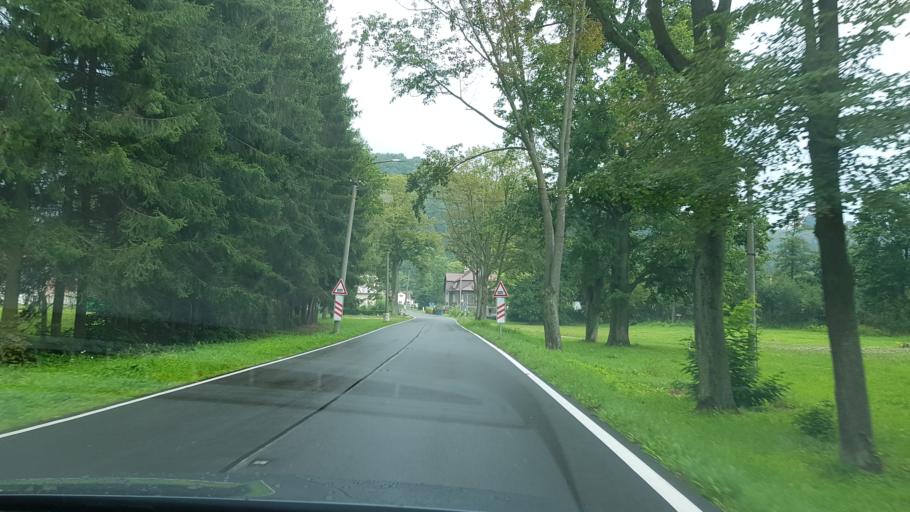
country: CZ
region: Olomoucky
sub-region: Okres Sumperk
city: Hanusovice
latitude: 50.0793
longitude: 16.9296
